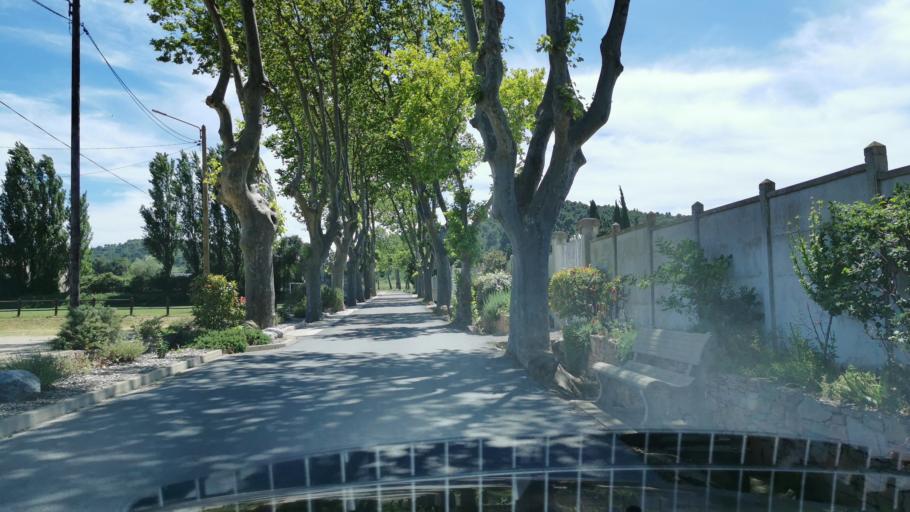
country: FR
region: Languedoc-Roussillon
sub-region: Departement de l'Aude
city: Nevian
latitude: 43.2090
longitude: 2.9038
